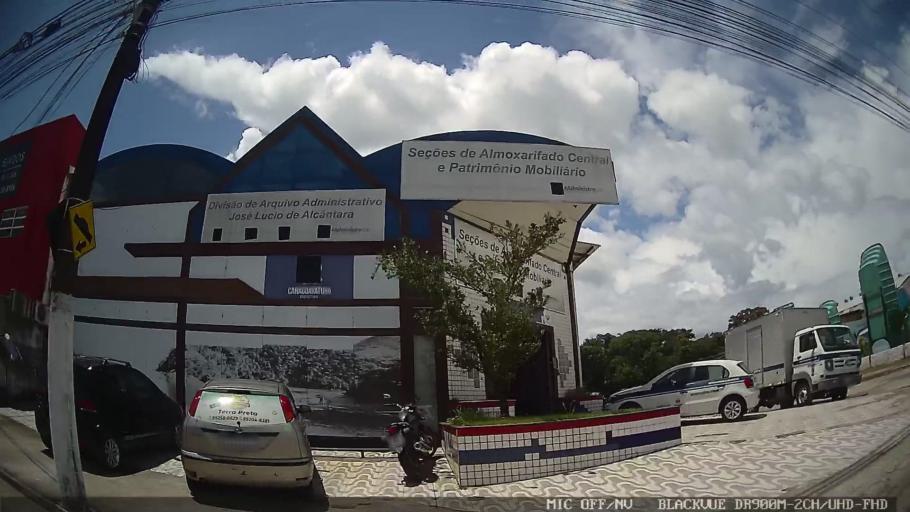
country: BR
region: Sao Paulo
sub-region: Caraguatatuba
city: Caraguatatuba
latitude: -23.6511
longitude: -45.4329
